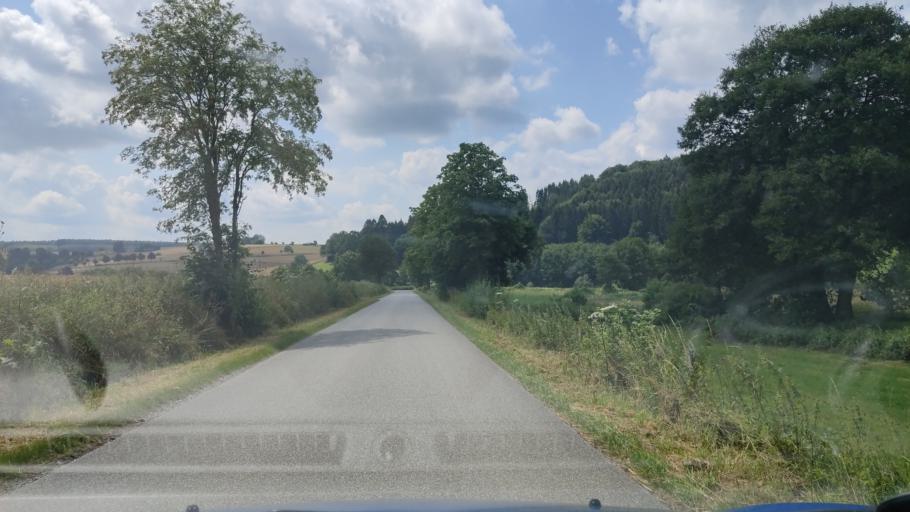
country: DE
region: Lower Saxony
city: Bodenfelde
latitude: 51.7031
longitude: 9.5536
